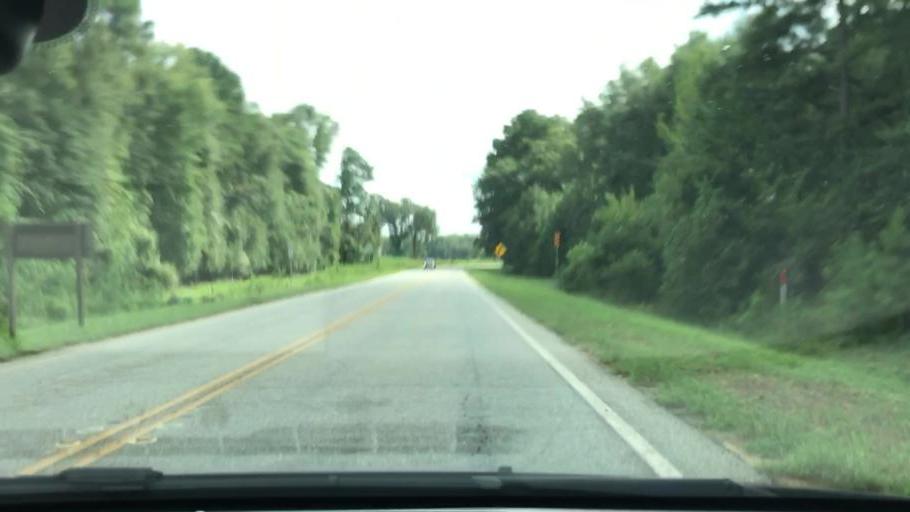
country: US
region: Georgia
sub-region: Clay County
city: Fort Gaines
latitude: 31.6907
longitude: -85.0465
